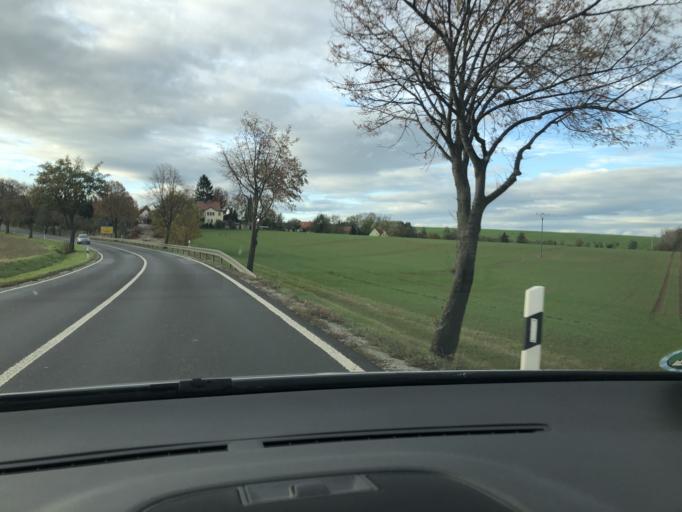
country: DE
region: Thuringia
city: Frankendorf
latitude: 50.9663
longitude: 11.4556
